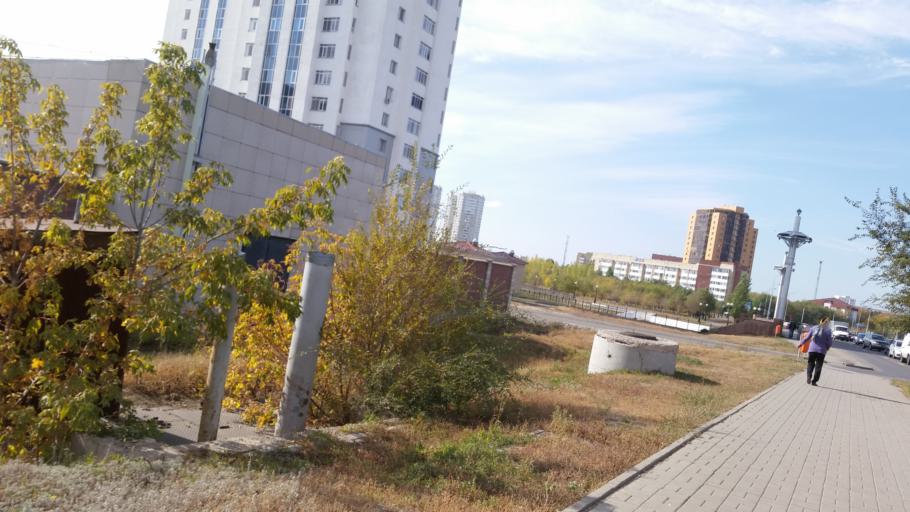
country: KZ
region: Astana Qalasy
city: Astana
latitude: 51.1640
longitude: 71.4791
